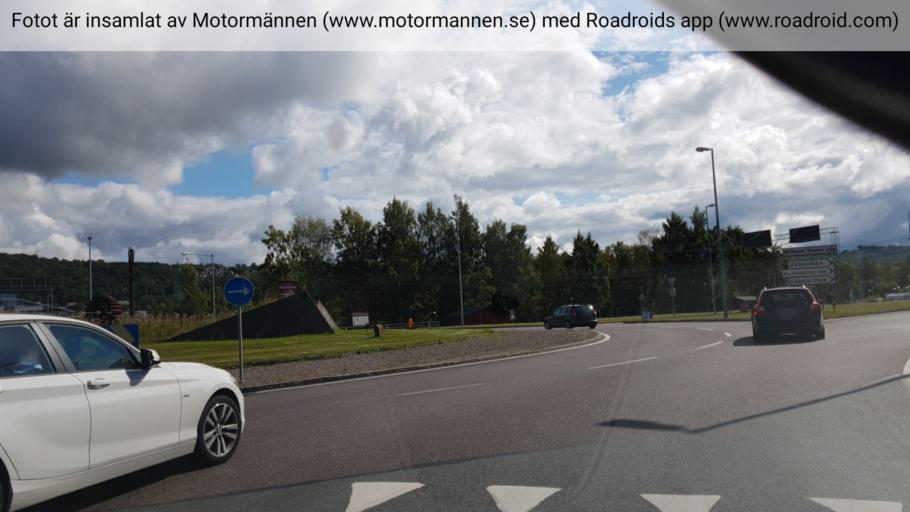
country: SE
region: Joenkoeping
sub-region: Jonkopings Kommun
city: Huskvarna
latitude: 57.7885
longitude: 14.2657
